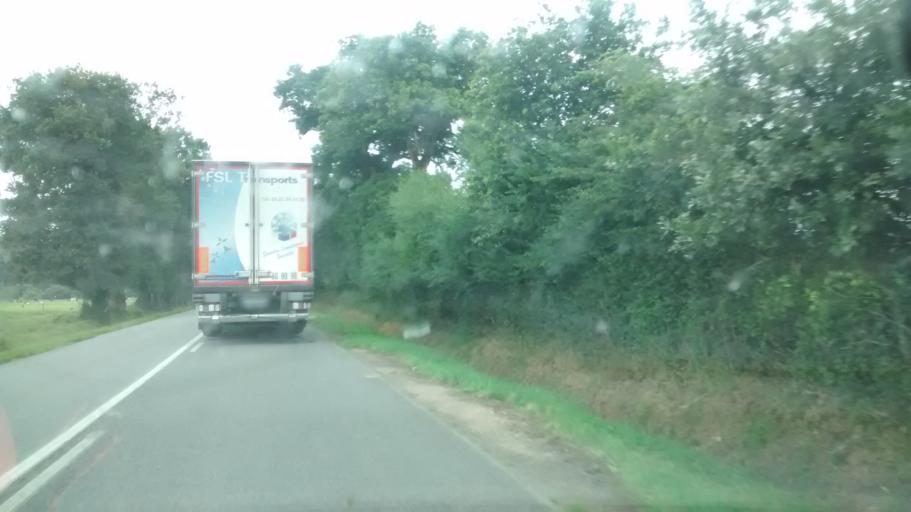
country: FR
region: Brittany
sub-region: Departement du Morbihan
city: Malestroit
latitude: 47.7907
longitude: -2.4221
